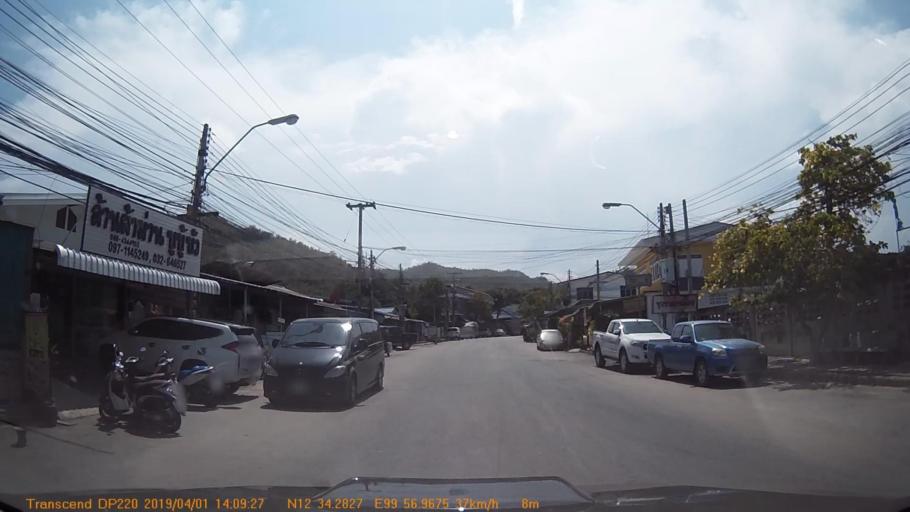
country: TH
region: Prachuap Khiri Khan
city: Hua Hin
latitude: 12.5713
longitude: 99.9492
